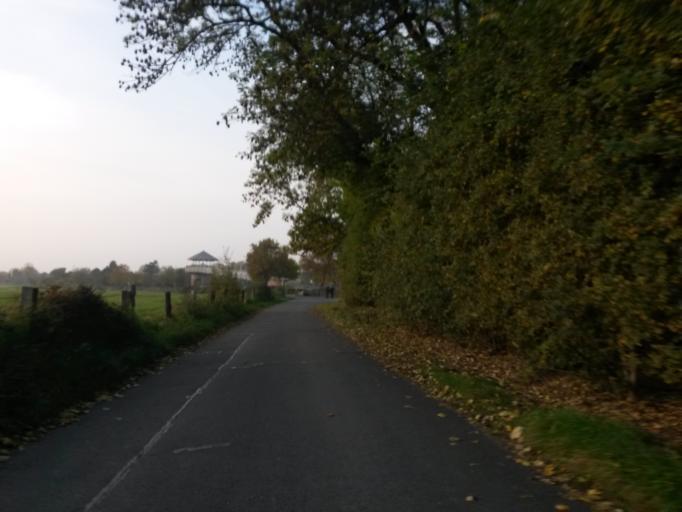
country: DE
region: Bremen
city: Bremen
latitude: 53.0572
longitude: 8.8662
